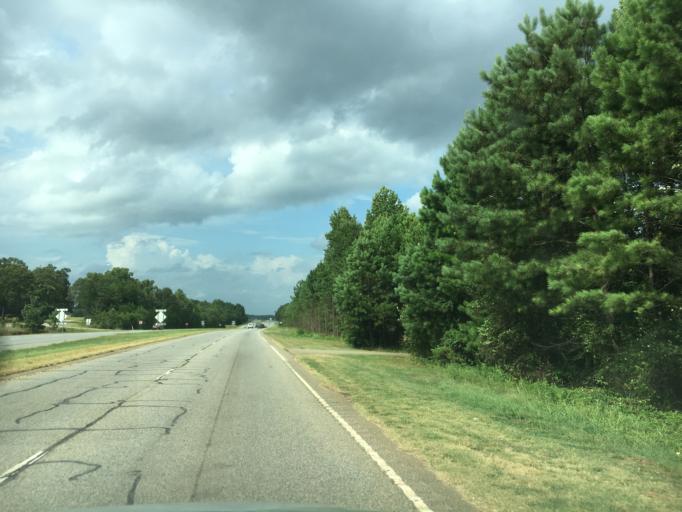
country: US
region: South Carolina
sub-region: Anderson County
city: Piedmont
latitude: 34.6680
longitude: -82.5141
